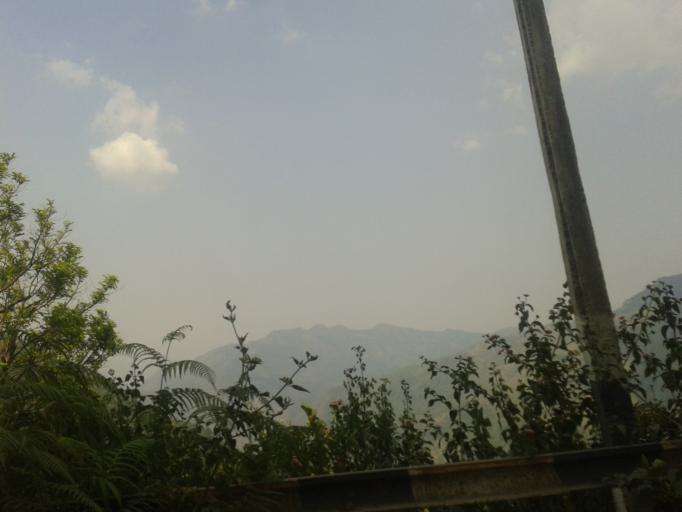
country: IN
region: Tamil Nadu
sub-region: Dindigul
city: Kodaikanal
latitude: 10.3305
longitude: 77.5648
